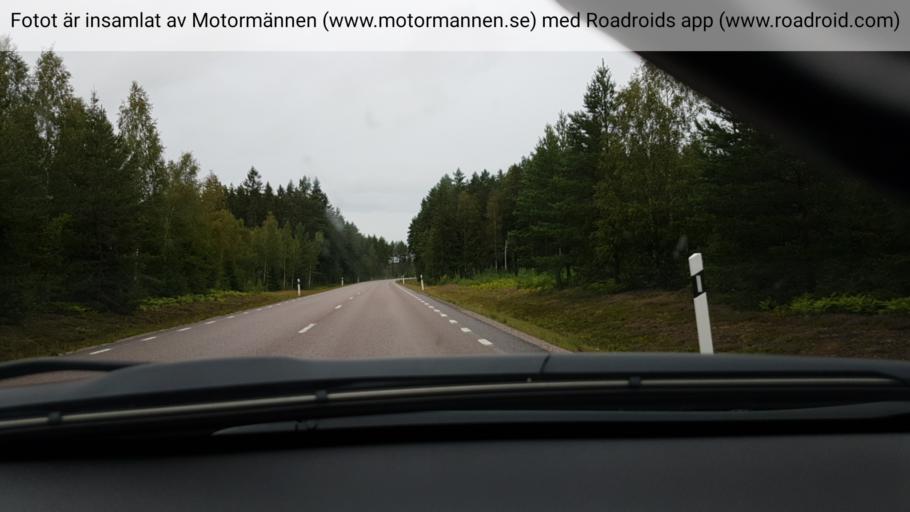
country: SE
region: Gaevleborg
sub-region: Gavle Kommun
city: Hedesunda
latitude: 60.4029
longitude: 16.9738
